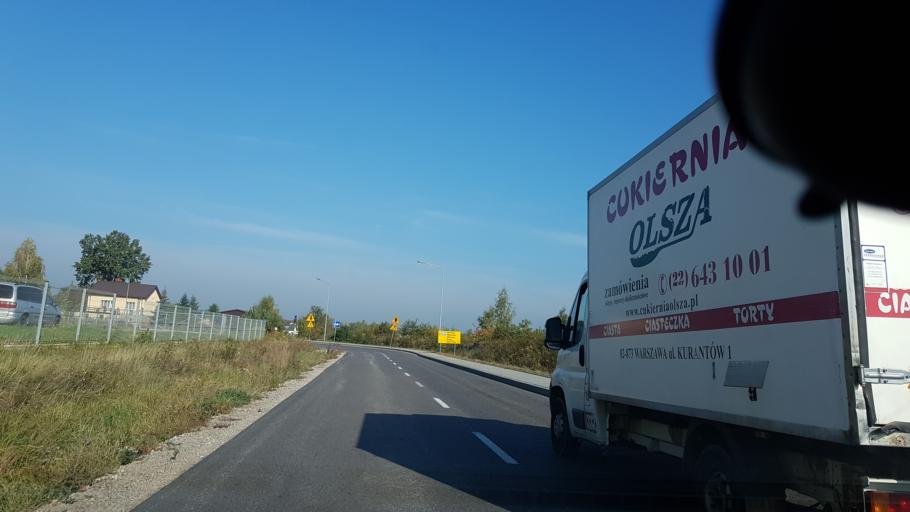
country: PL
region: Masovian Voivodeship
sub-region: Powiat pruszkowski
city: Nadarzyn
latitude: 52.0758
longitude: 20.7730
